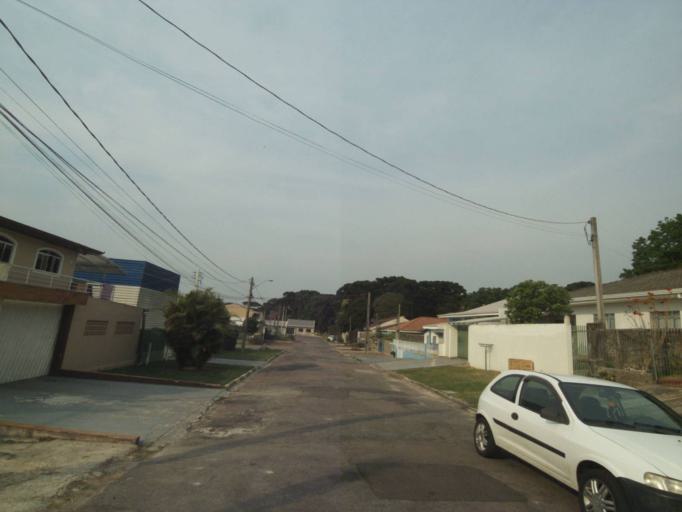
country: BR
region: Parana
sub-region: Sao Jose Dos Pinhais
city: Sao Jose dos Pinhais
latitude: -25.5271
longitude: -49.2821
